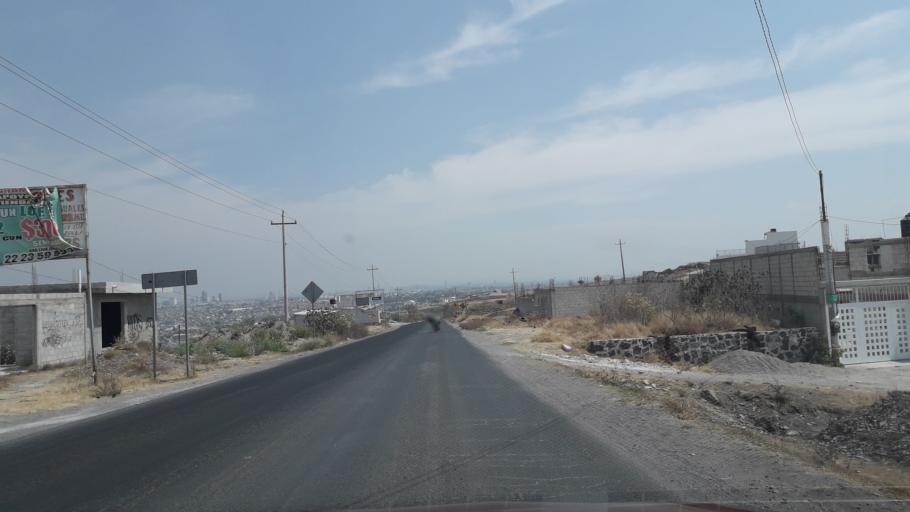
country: MX
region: Puebla
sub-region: Puebla
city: El Capulo (La Quebradora)
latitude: 18.9391
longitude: -98.2707
